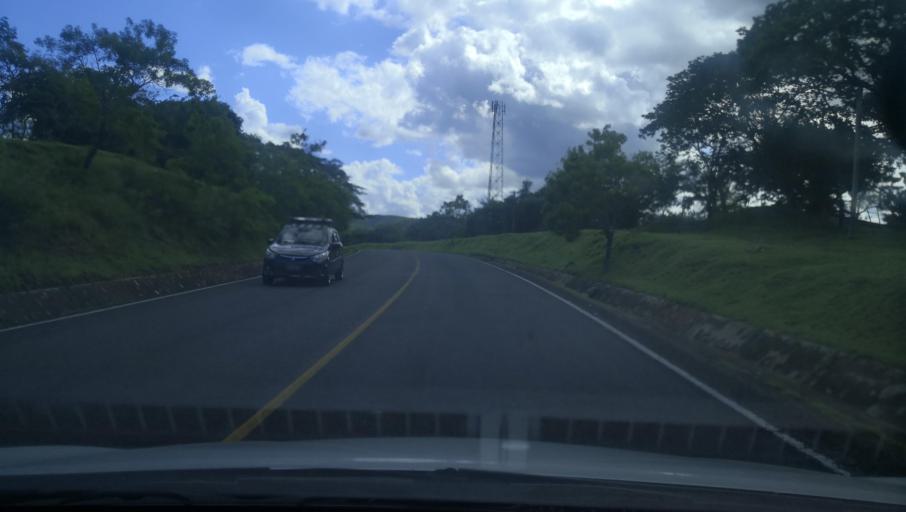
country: NI
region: Madriz
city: Somoto
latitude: 13.4673
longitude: -86.6526
